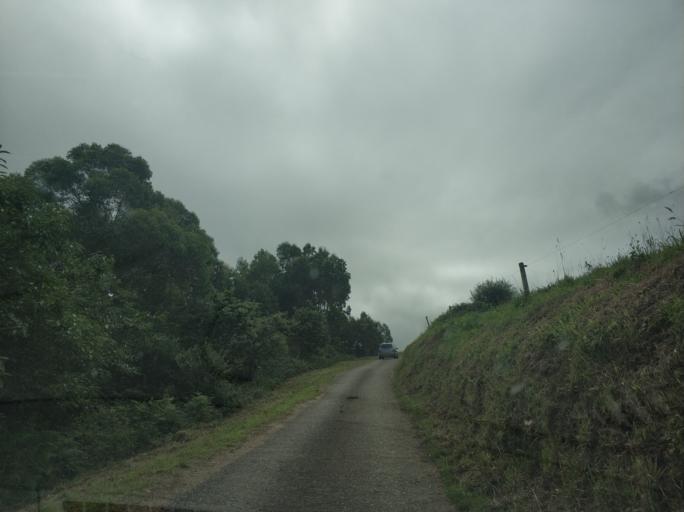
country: ES
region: Asturias
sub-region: Province of Asturias
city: Cudillero
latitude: 43.5659
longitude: -6.2937
